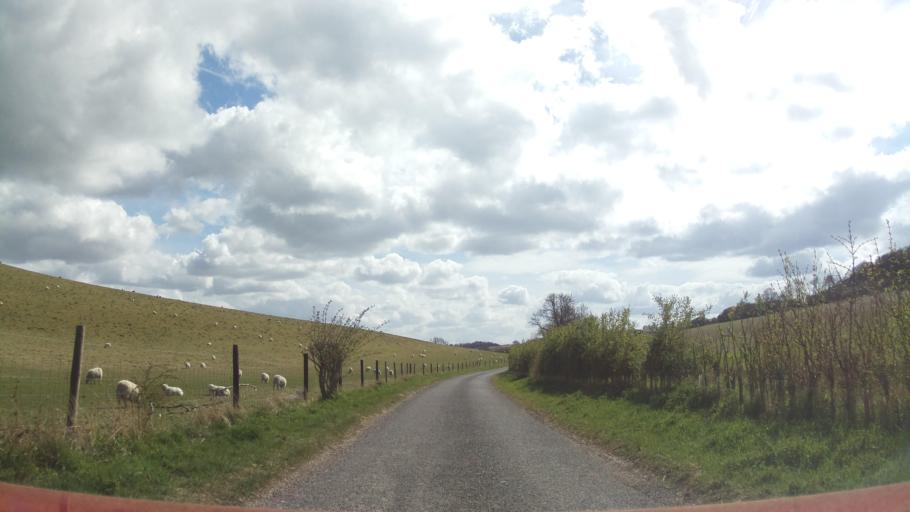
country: GB
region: England
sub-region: West Berkshire
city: Kintbury
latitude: 51.3372
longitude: -1.4699
